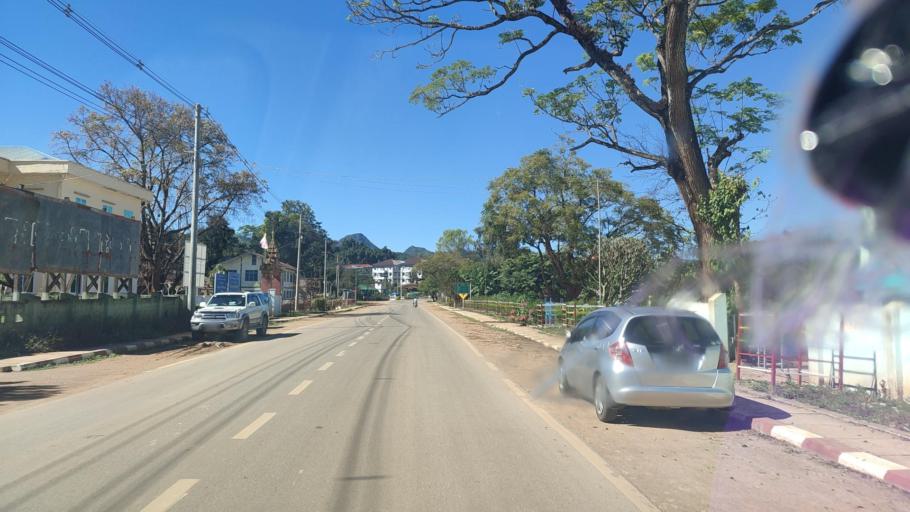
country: MM
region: Shan
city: Taunggyi
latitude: 20.9192
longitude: 97.5675
